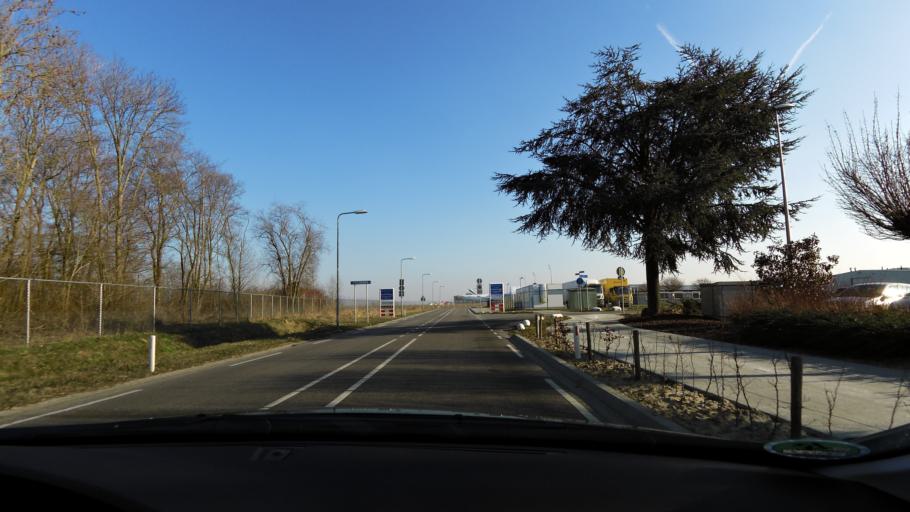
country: NL
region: Limburg
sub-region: Gemeente Meerssen
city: Meerssen
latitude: 50.9103
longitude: 5.7735
